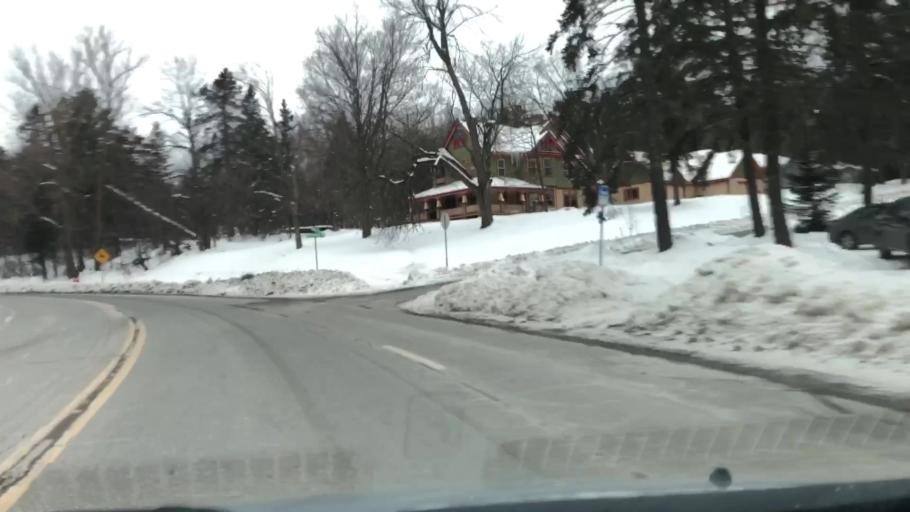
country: US
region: Minnesota
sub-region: Saint Louis County
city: Arnold
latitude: 46.8387
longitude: -92.0759
